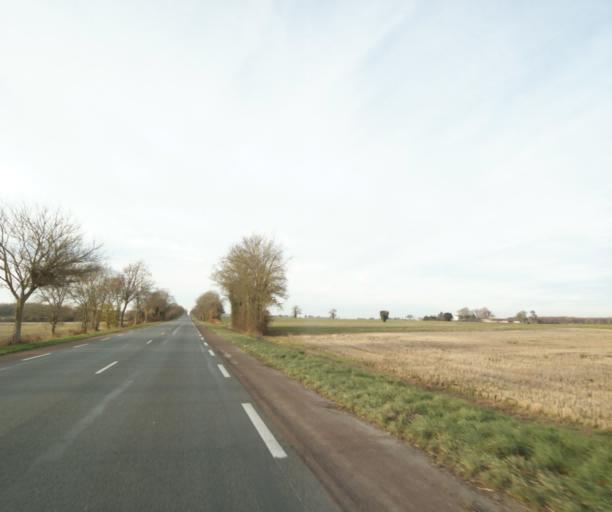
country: FR
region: Poitou-Charentes
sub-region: Departement de la Charente-Maritime
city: Saint-Georges-des-Coteaux
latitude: 45.7951
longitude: -0.7340
